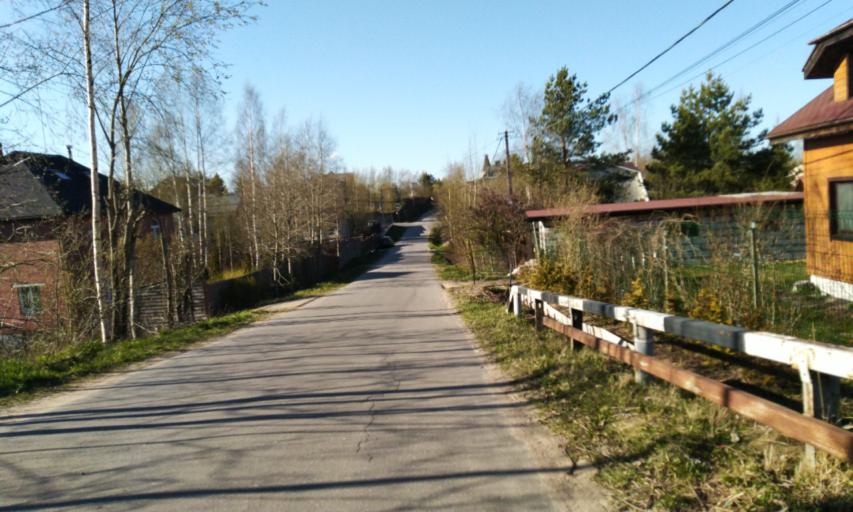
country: RU
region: Leningrad
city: Toksovo
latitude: 60.1474
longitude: 30.5690
